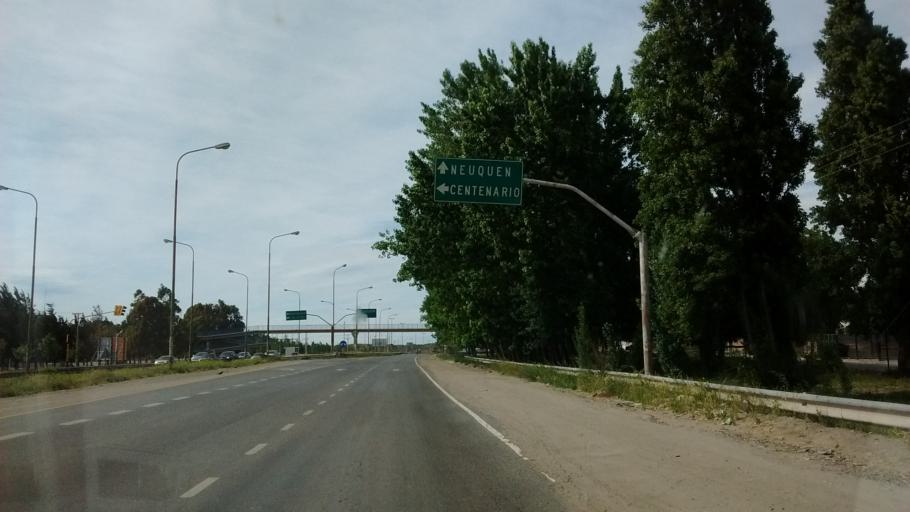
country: AR
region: Neuquen
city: Neuquen
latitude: -38.9091
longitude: -68.0820
